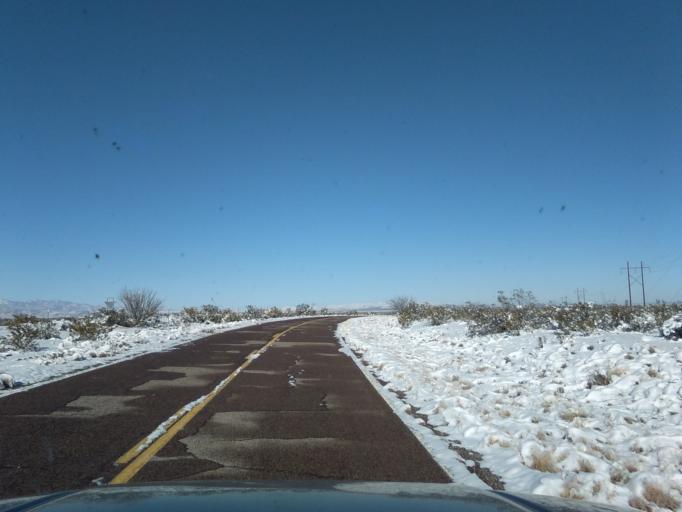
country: US
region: New Mexico
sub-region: Sierra County
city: Elephant Butte
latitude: 33.6134
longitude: -107.1468
